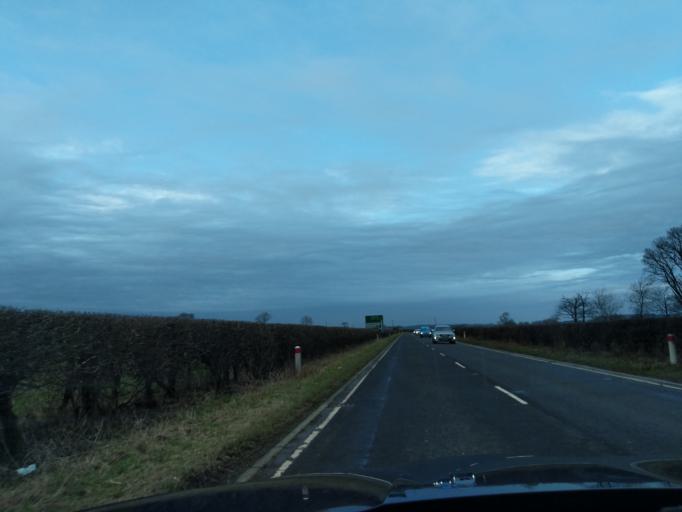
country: GB
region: England
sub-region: Northumberland
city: Hartburn
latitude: 55.1079
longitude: -1.8566
